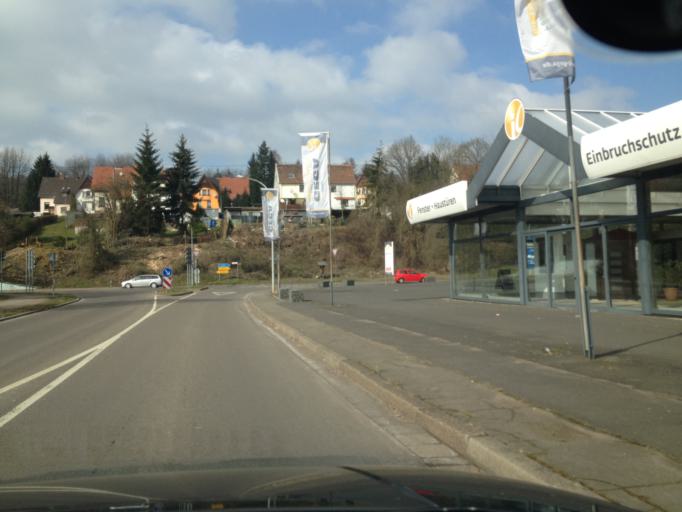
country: DE
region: Saarland
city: Schiffweiler
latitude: 49.3522
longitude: 7.1101
